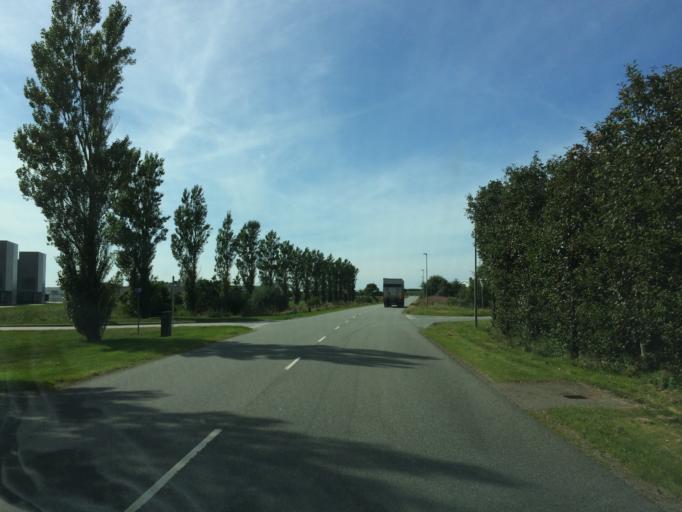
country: DK
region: Central Jutland
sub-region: Ringkobing-Skjern Kommune
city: Skjern
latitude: 56.0218
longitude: 8.3800
